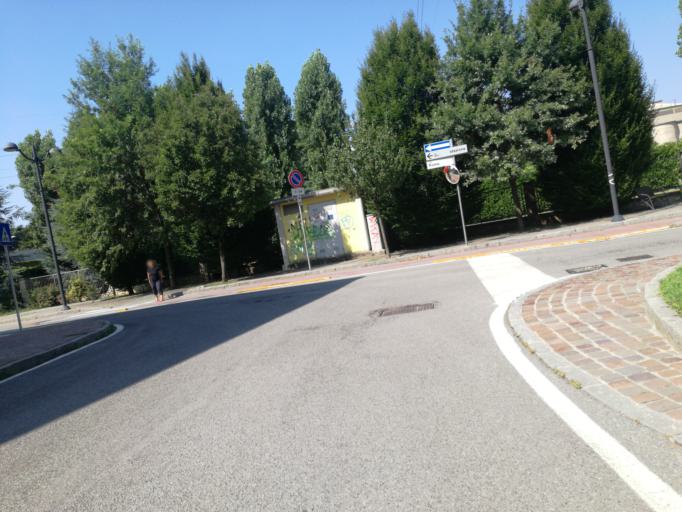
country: IT
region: Lombardy
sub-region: Provincia di Bergamo
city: Calusco d'Adda
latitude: 45.6857
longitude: 9.4711
